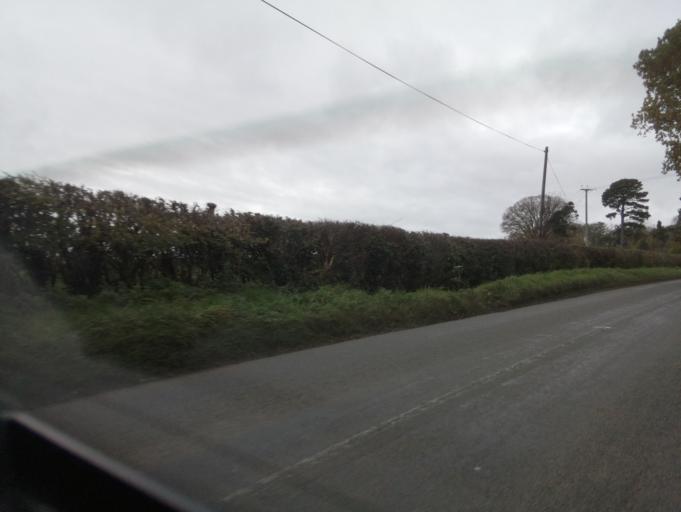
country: GB
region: England
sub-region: Somerset
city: Yeovil
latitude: 50.9952
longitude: -2.5807
